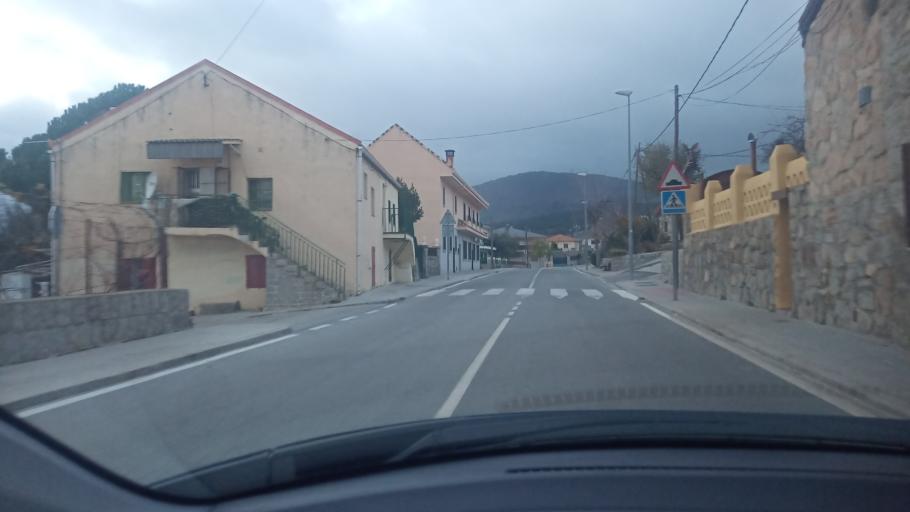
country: ES
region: Madrid
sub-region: Provincia de Madrid
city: Zarzalejo
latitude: 40.5400
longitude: -4.1661
